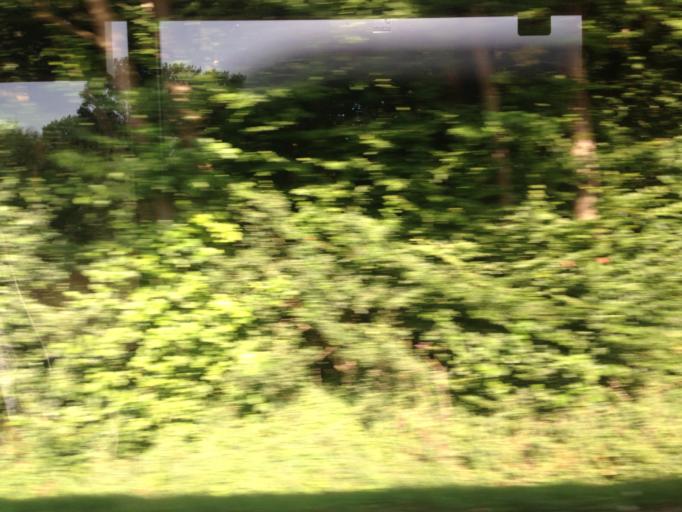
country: DE
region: North Rhine-Westphalia
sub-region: Regierungsbezirk Munster
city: Senden
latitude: 51.8738
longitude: 7.4930
